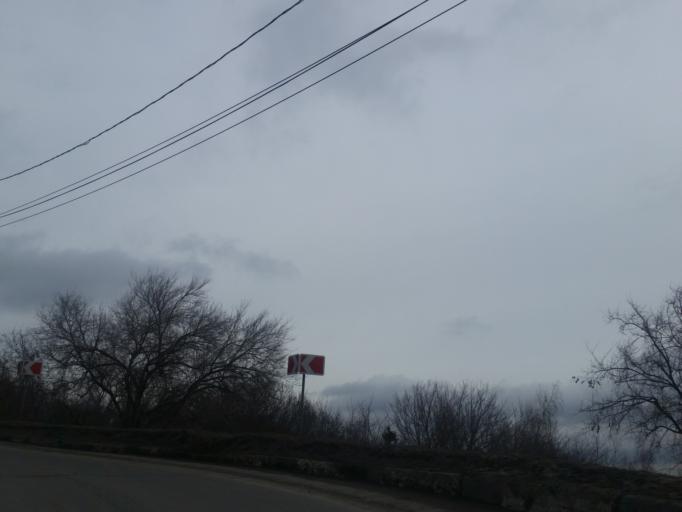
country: RU
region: Ulyanovsk
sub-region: Ulyanovskiy Rayon
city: Ulyanovsk
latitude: 54.3096
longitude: 48.4069
